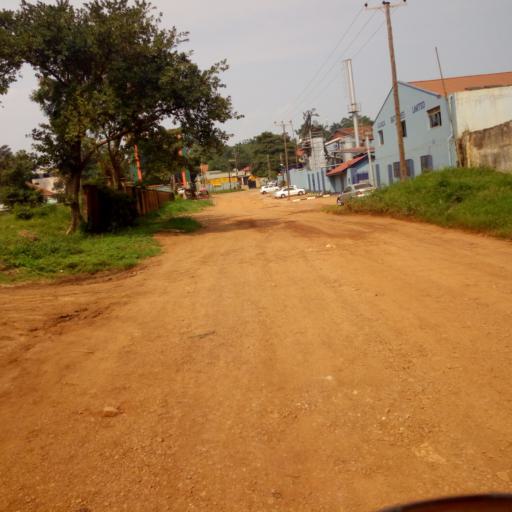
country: UG
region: Central Region
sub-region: Kampala District
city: Kampala
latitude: 0.3170
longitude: 32.6161
